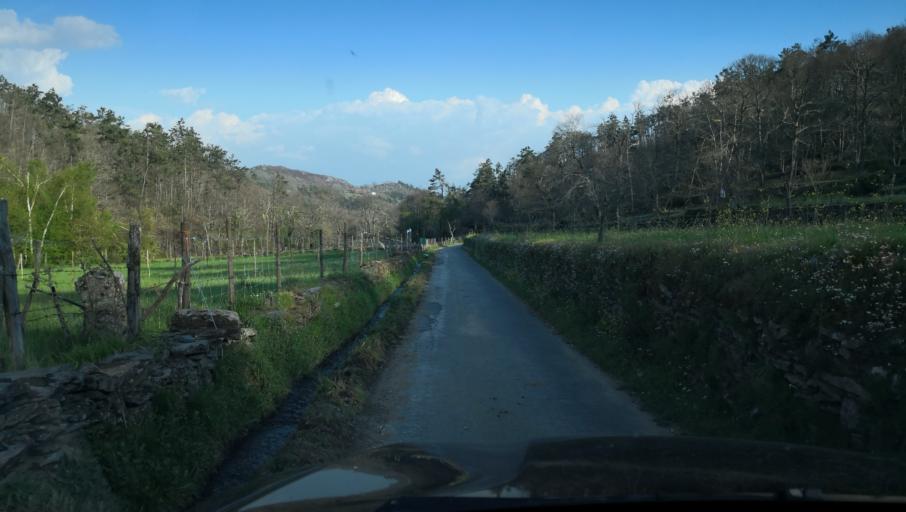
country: PT
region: Vila Real
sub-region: Vila Real
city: Vila Real
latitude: 41.3054
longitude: -7.8423
